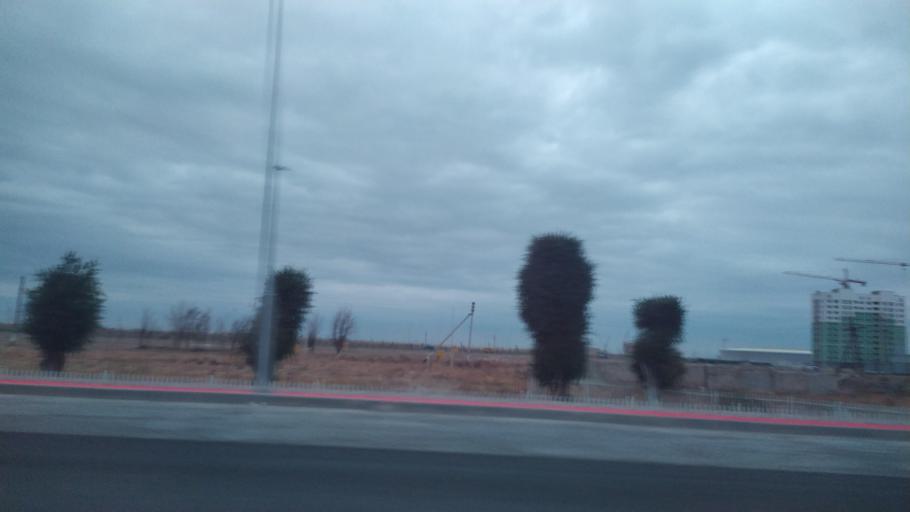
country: KZ
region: Ongtustik Qazaqstan
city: Turkestan
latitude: 43.2695
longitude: 68.3519
